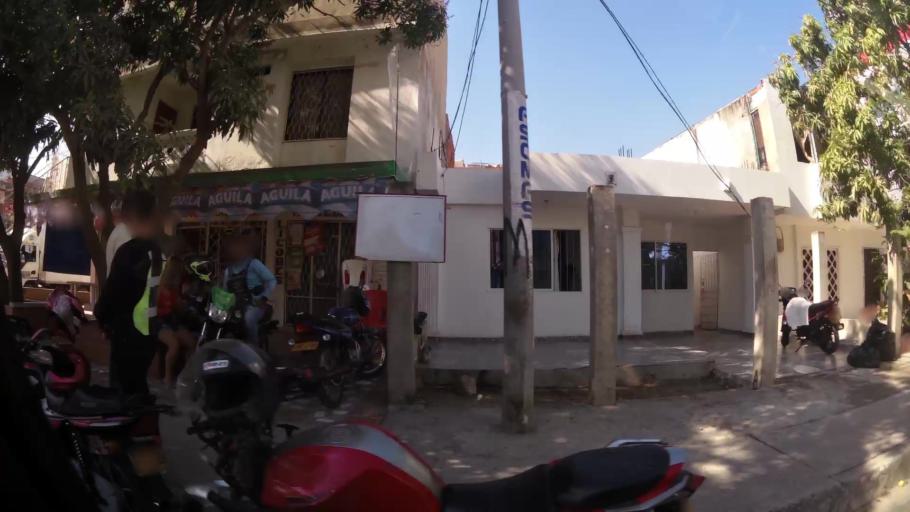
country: CO
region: Bolivar
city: Cartagena
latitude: 10.3940
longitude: -75.4734
